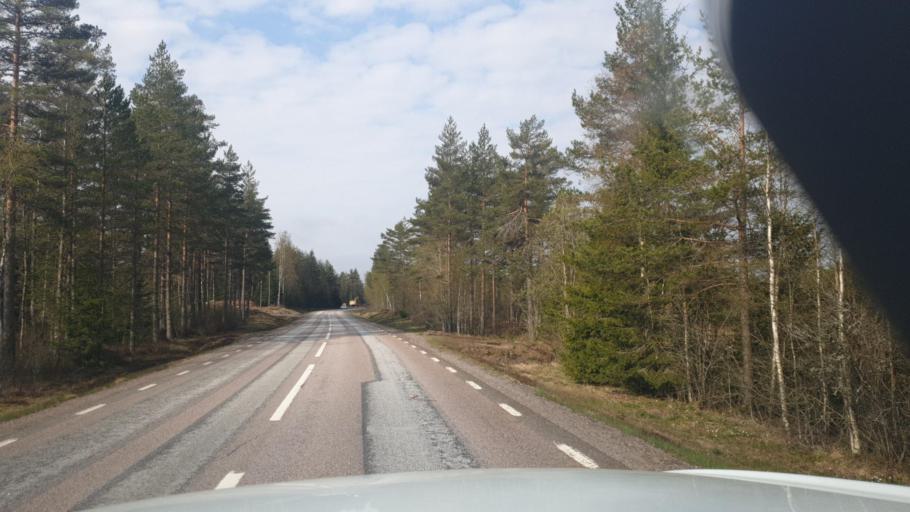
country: SE
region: Vaermland
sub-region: Sunne Kommun
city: Sunne
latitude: 59.6961
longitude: 13.0932
